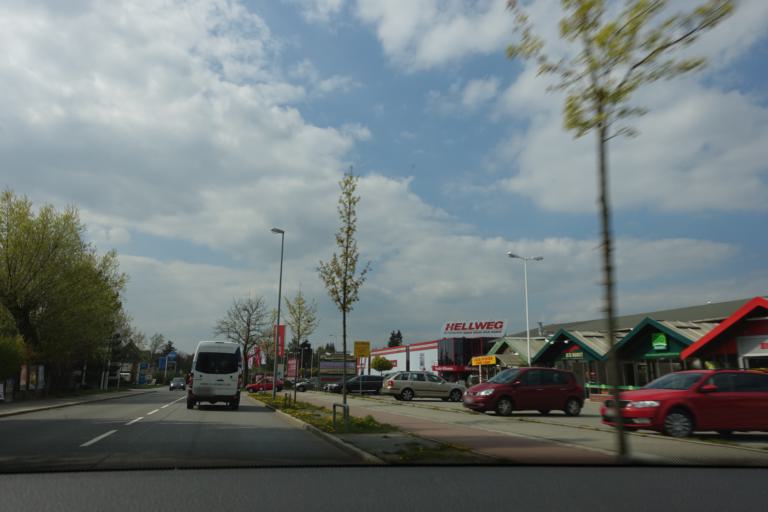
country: DE
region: Saxony
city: Chemnitz
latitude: 50.8139
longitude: 12.9562
